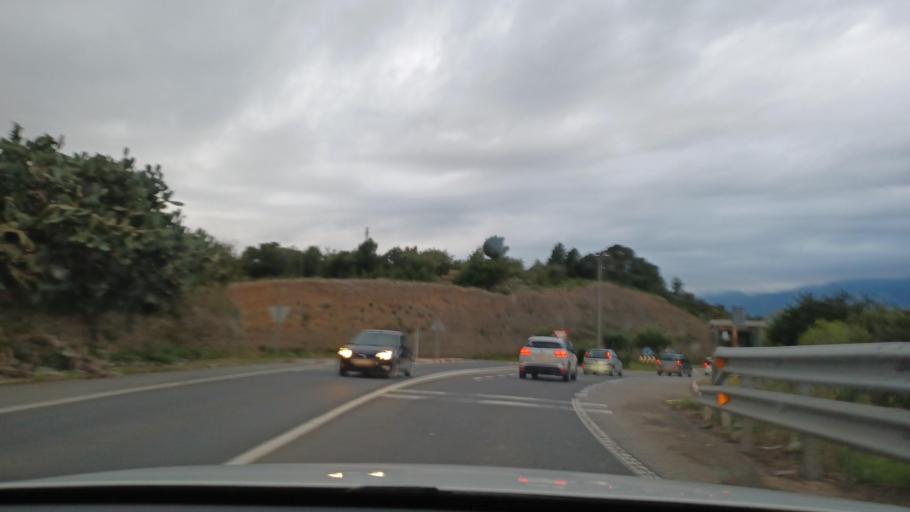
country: ES
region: Catalonia
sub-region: Provincia de Tarragona
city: Tortosa
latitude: 40.7758
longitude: 0.5123
